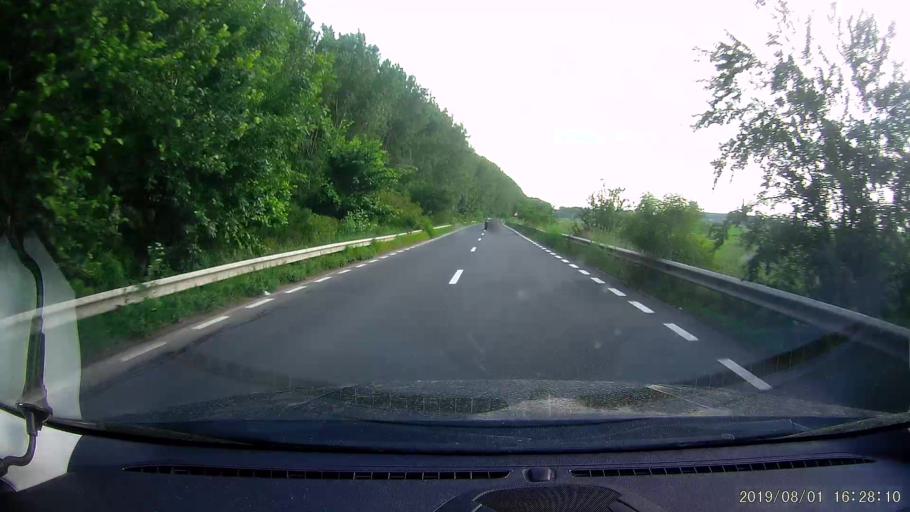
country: RO
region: Calarasi
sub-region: Municipiul Calarasi
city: Calarasi
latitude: 44.1519
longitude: 27.3127
